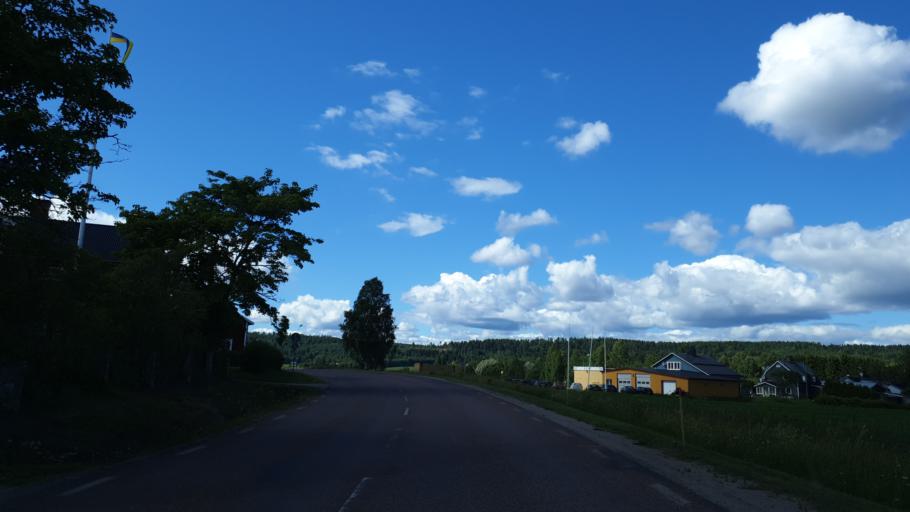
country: SE
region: Gaevleborg
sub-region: Nordanstigs Kommun
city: Bergsjoe
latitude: 62.0483
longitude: 17.2377
